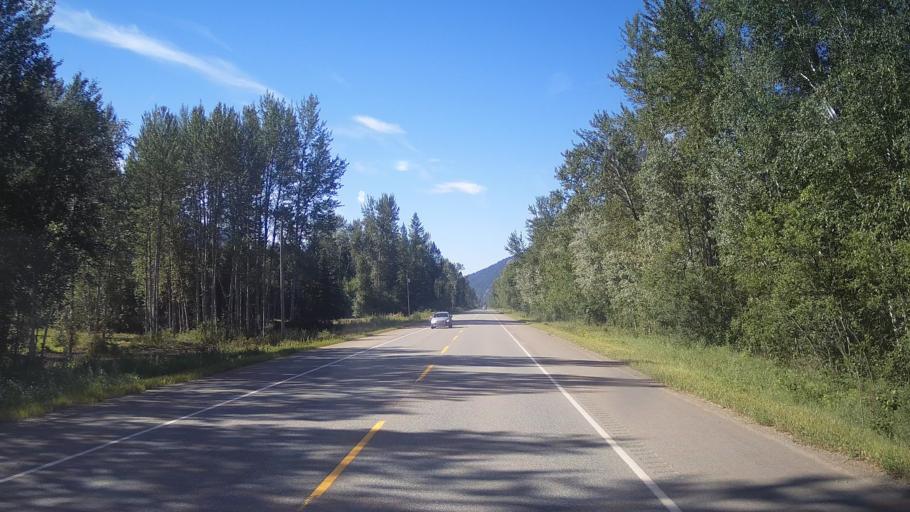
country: CA
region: British Columbia
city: Chase
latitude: 51.5205
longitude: -120.1722
